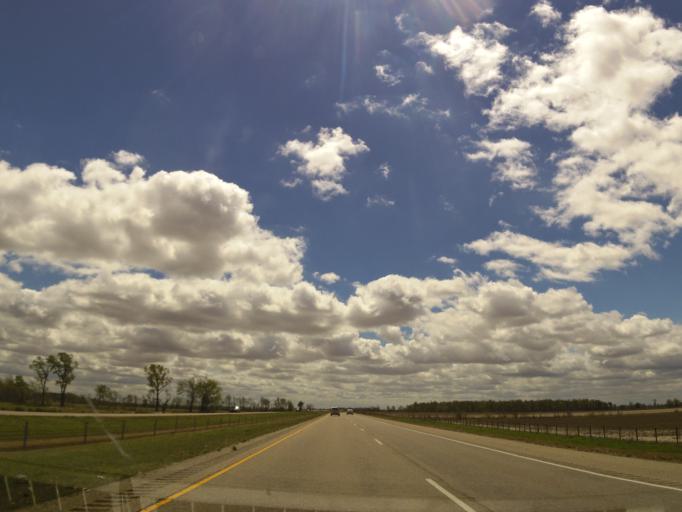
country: US
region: Arkansas
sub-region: Craighead County
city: Bay
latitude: 35.7289
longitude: -90.5801
